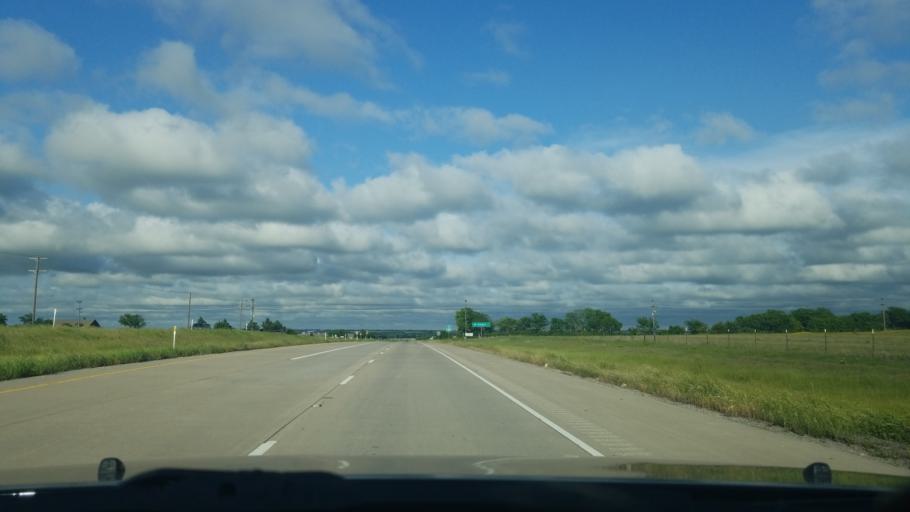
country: US
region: Texas
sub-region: Wise County
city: New Fairview
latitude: 33.2492
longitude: -97.4312
